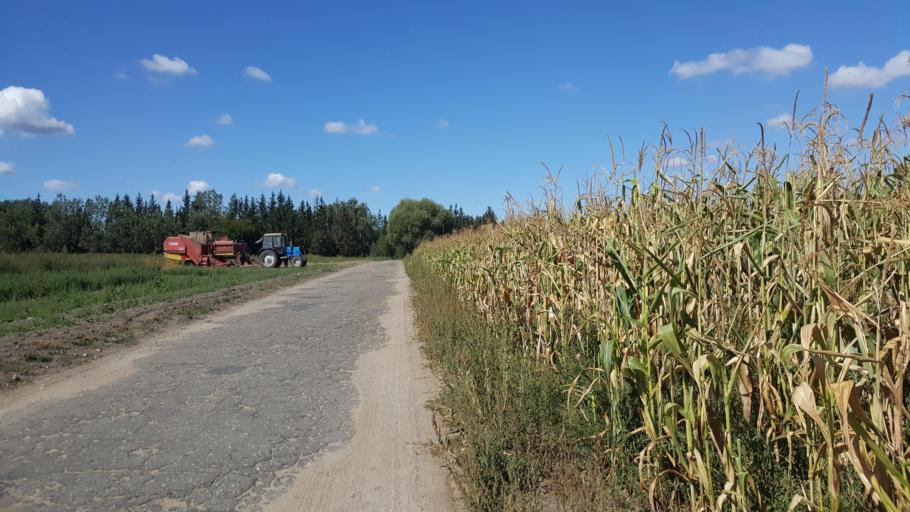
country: BY
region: Brest
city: Vysokaye
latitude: 52.3364
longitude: 23.3376
